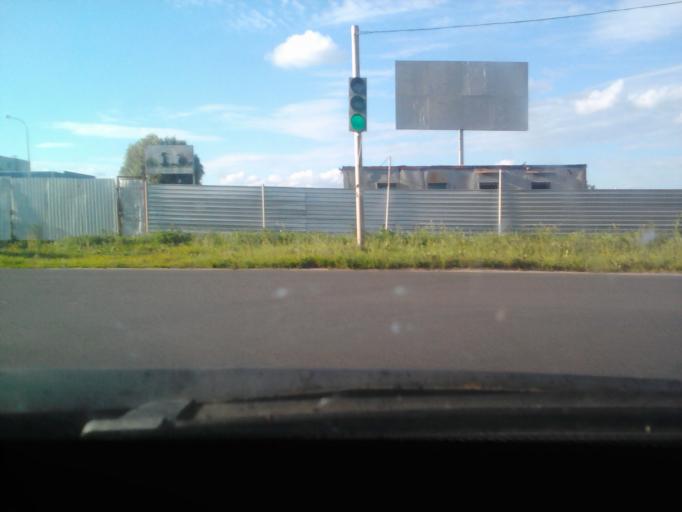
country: RU
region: Kursk
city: Kurchatov
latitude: 51.6585
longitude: 35.6756
